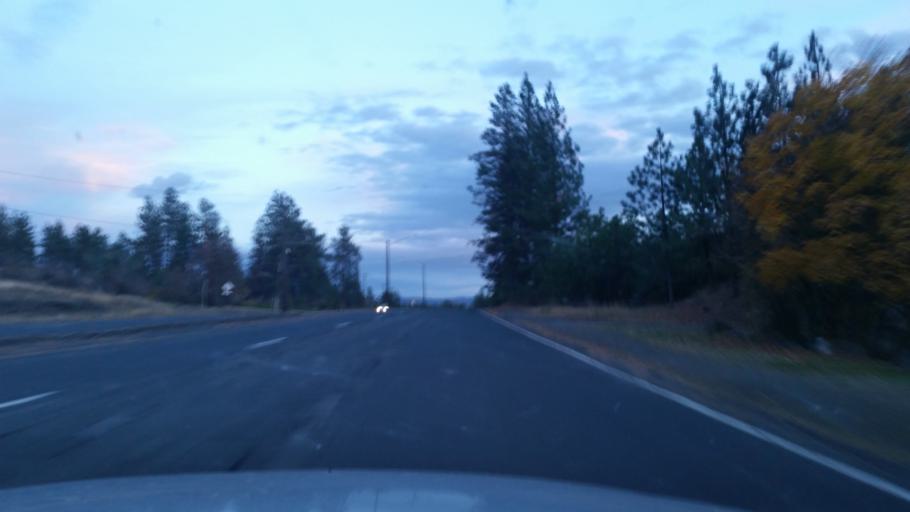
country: US
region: Washington
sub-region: Spokane County
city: Spokane
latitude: 47.6415
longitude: -117.4807
